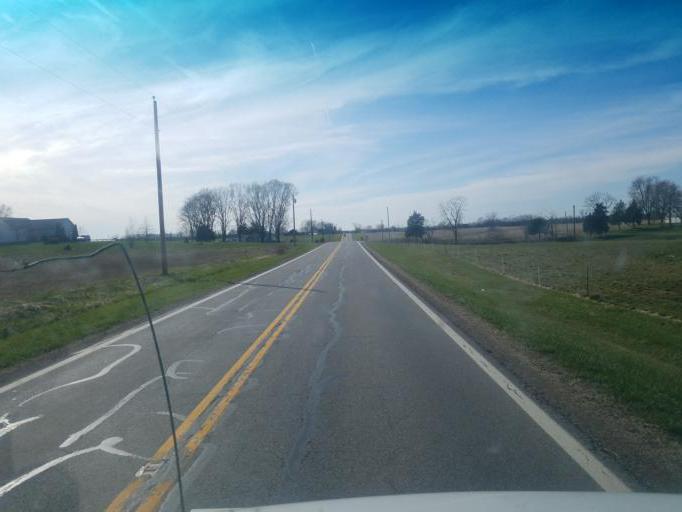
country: US
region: Ohio
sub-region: Champaign County
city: North Lewisburg
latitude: 40.3440
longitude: -83.4963
